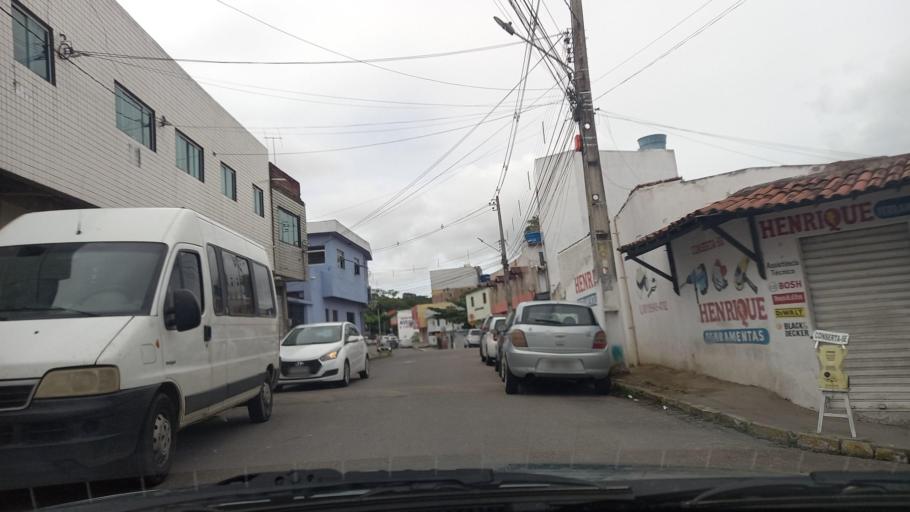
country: BR
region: Pernambuco
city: Garanhuns
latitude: -8.8932
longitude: -36.4930
